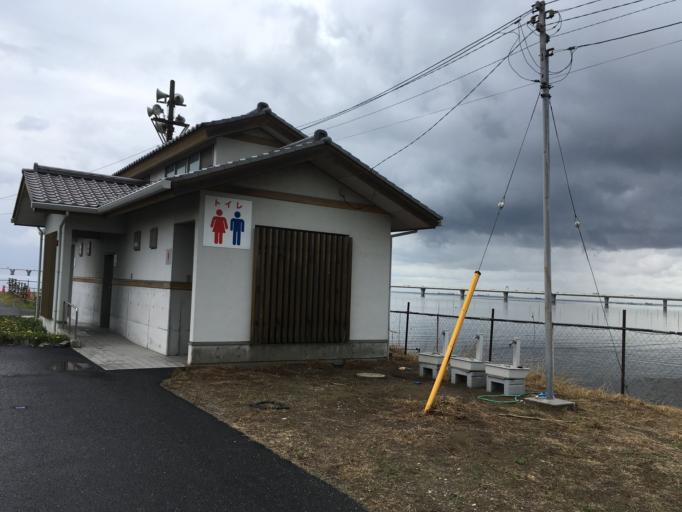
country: JP
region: Chiba
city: Kisarazu
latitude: 35.4318
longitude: 139.9051
